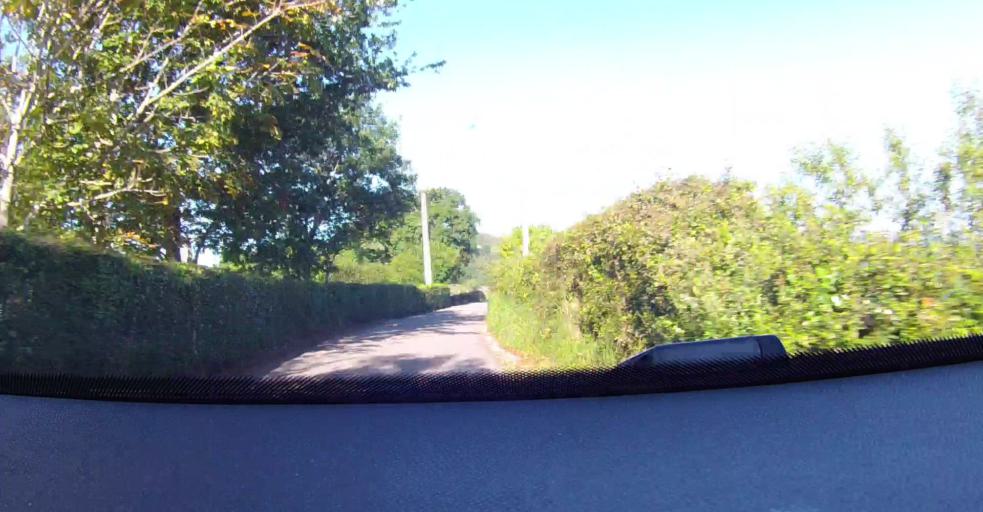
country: ES
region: Asturias
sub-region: Province of Asturias
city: Villaviciosa
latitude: 43.4860
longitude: -5.3961
